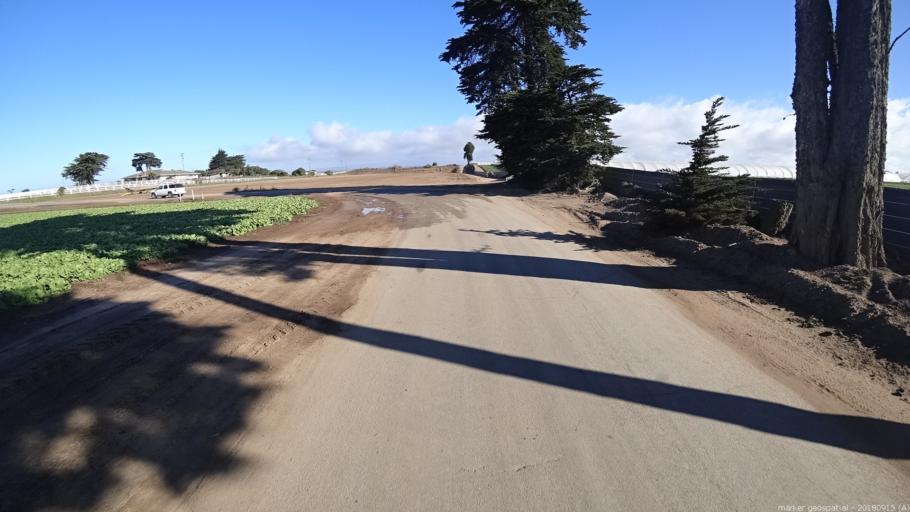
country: US
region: California
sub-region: Monterey County
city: Elkhorn
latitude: 36.8283
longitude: -121.7892
